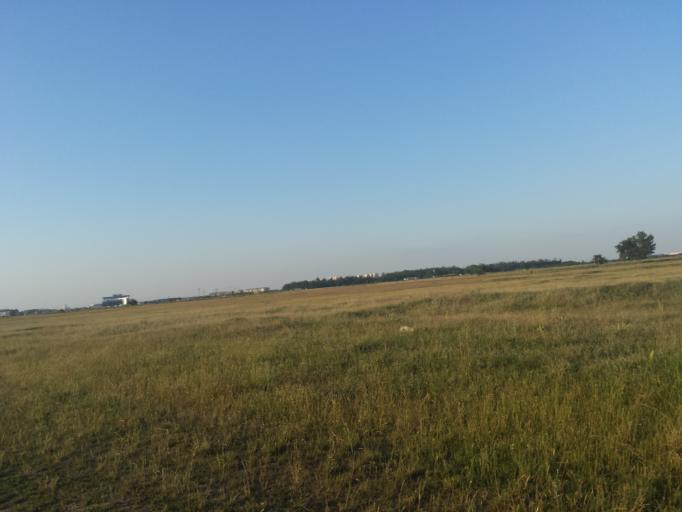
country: RO
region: Ilfov
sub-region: Comuna Tunari
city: Tunari
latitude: 44.5183
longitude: 26.1529
